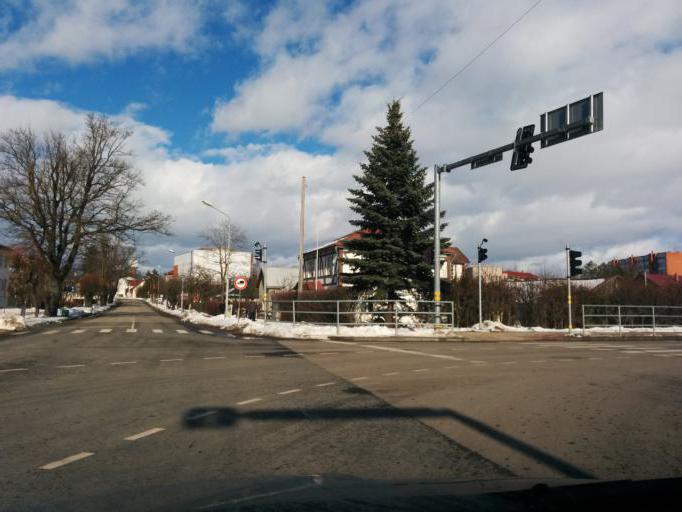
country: LV
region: Gulbenes Rajons
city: Gulbene
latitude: 57.1682
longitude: 26.7575
